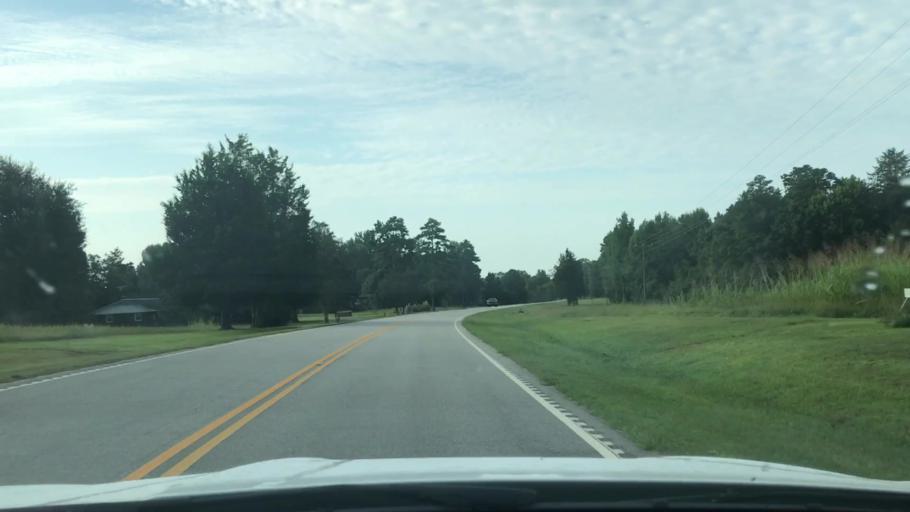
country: US
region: South Carolina
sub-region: Spartanburg County
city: Roebuck
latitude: 34.8292
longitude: -81.9237
